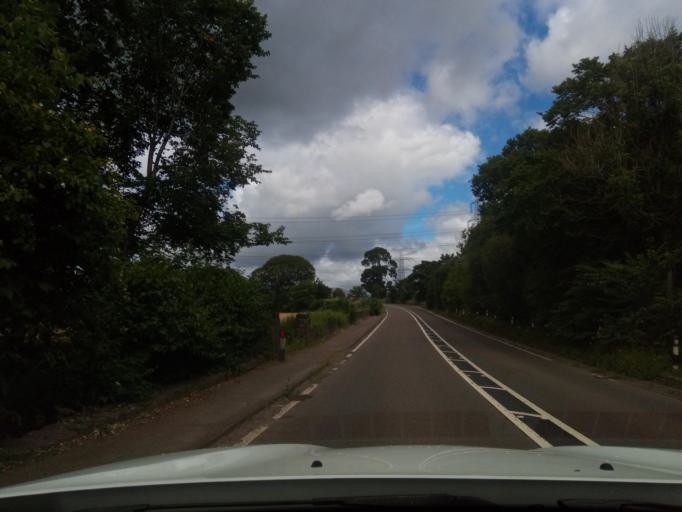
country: GB
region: Scotland
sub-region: Fife
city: Kincardine
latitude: 56.0853
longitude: -3.7201
